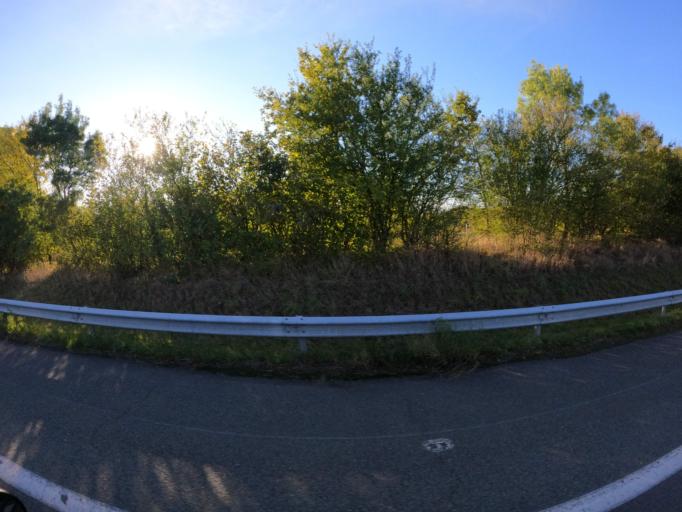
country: FR
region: Pays de la Loire
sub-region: Departement de Maine-et-Loire
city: Nuaille
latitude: 47.0817
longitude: -0.8251
